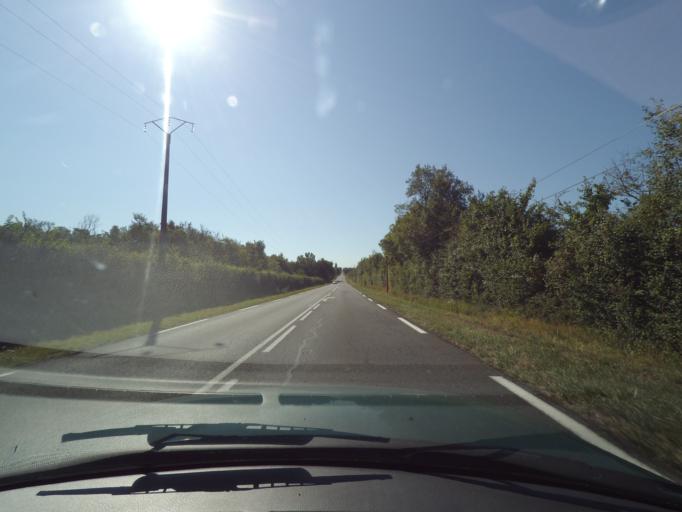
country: FR
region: Poitou-Charentes
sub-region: Departement de la Vienne
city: Lussac-les-Chateaux
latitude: 46.3684
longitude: 0.7663
